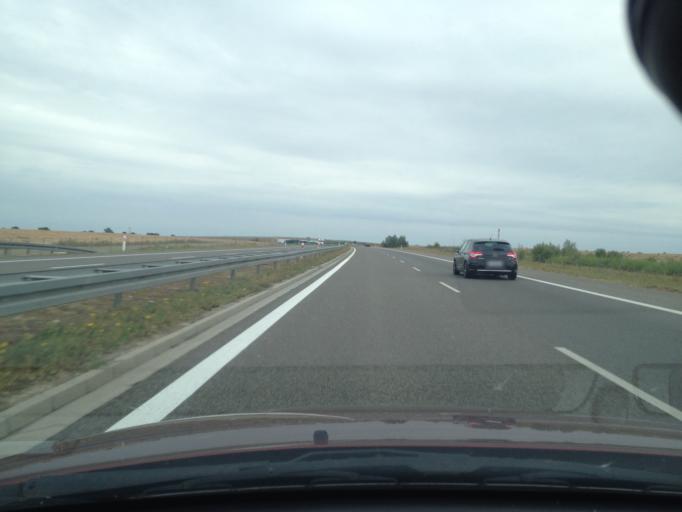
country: PL
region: Lubusz
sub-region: Powiat gorzowski
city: Jenin
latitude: 52.7687
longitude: 15.1291
